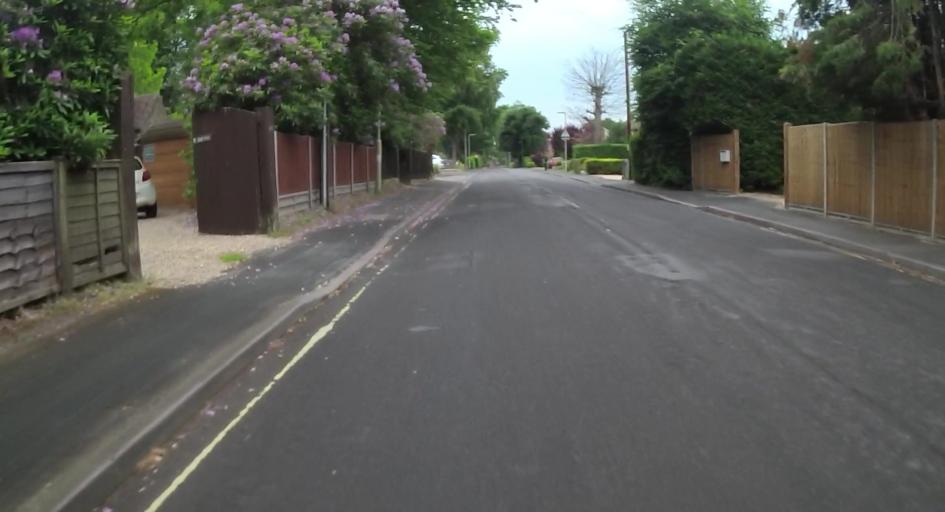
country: GB
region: England
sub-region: Hampshire
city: Fleet
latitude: 51.2788
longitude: -0.8332
